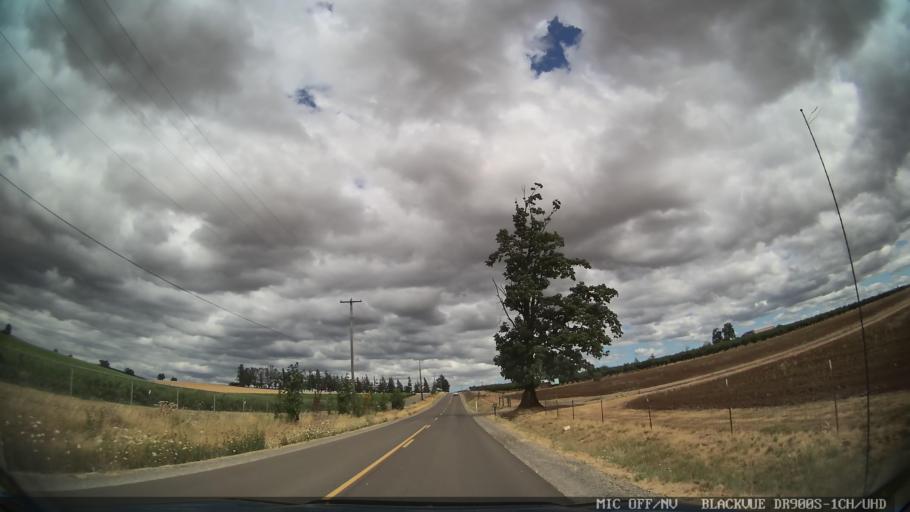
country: US
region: Oregon
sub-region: Marion County
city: Sublimity
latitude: 44.8662
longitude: -122.7712
